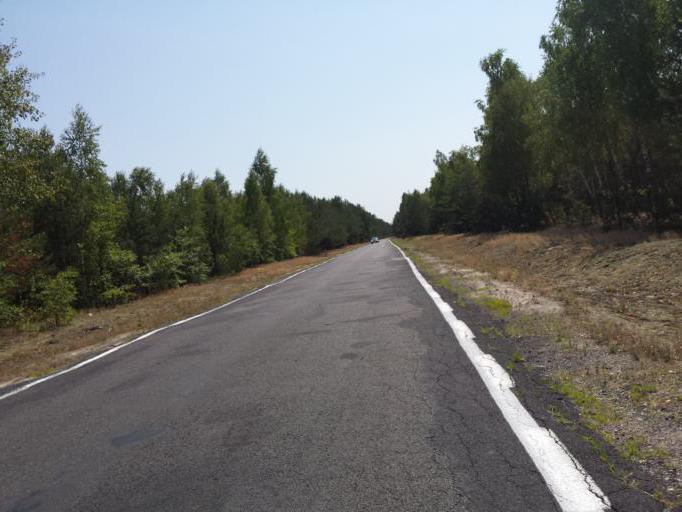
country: PL
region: Lublin Voivodeship
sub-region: Powiat bialski
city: Koden
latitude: 51.8697
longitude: 23.5956
